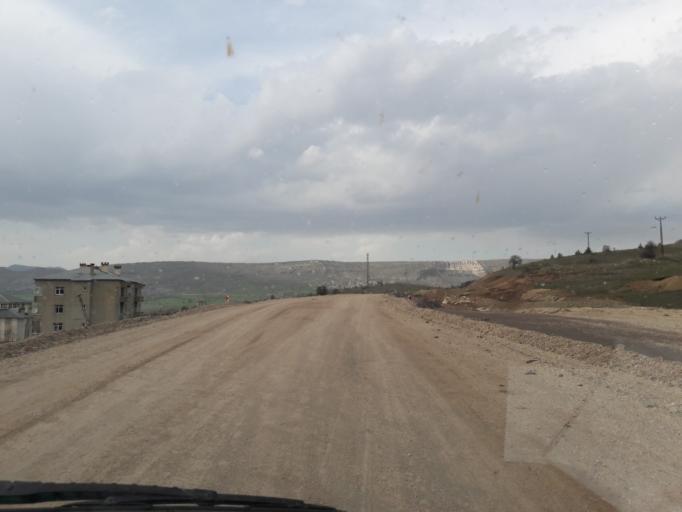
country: TR
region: Giresun
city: Alucra
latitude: 40.3164
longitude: 38.7720
